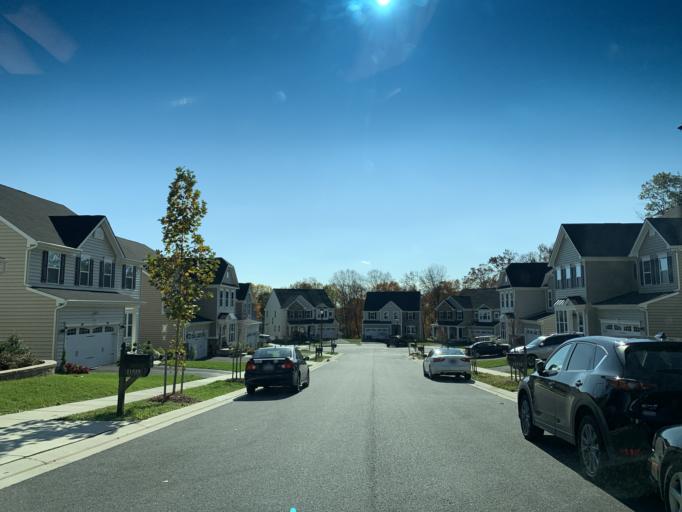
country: US
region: Maryland
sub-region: Baltimore County
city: White Marsh
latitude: 39.3999
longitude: -76.4155
